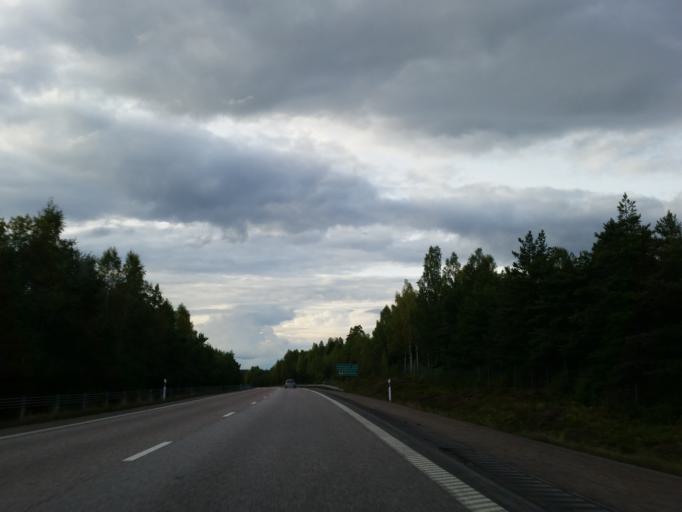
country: SE
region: Stockholm
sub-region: Sigtuna Kommun
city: Marsta
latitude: 59.6976
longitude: 17.8638
